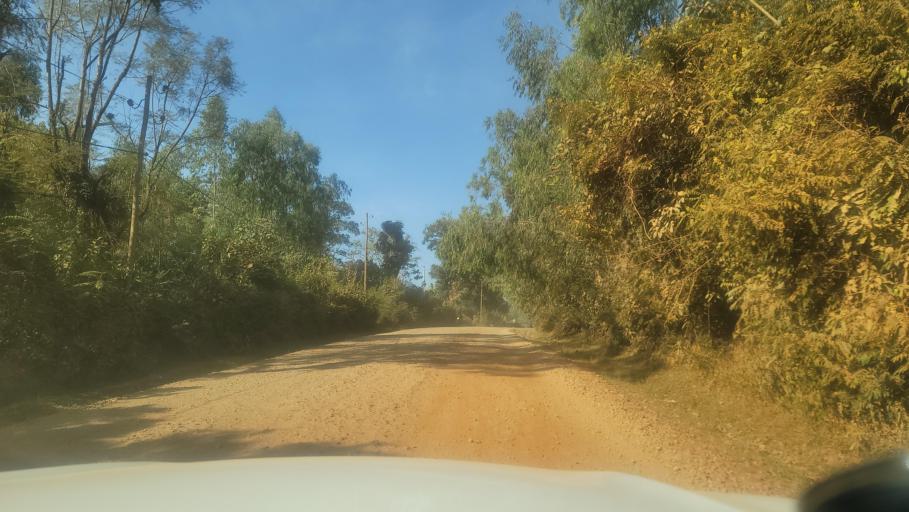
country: ET
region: Oromiya
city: Agaro
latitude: 7.8399
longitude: 36.5472
